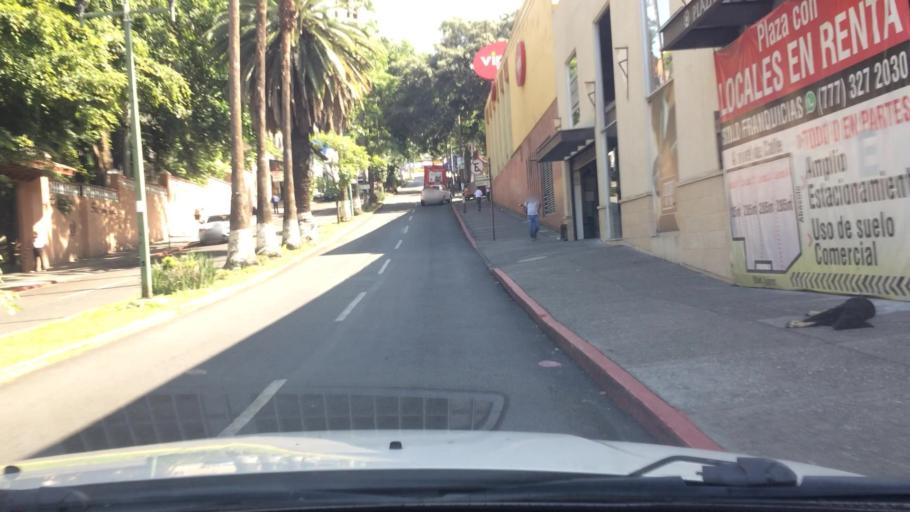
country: MX
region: Morelos
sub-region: Cuernavaca
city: Cuernavaca
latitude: 18.9189
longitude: -99.2337
